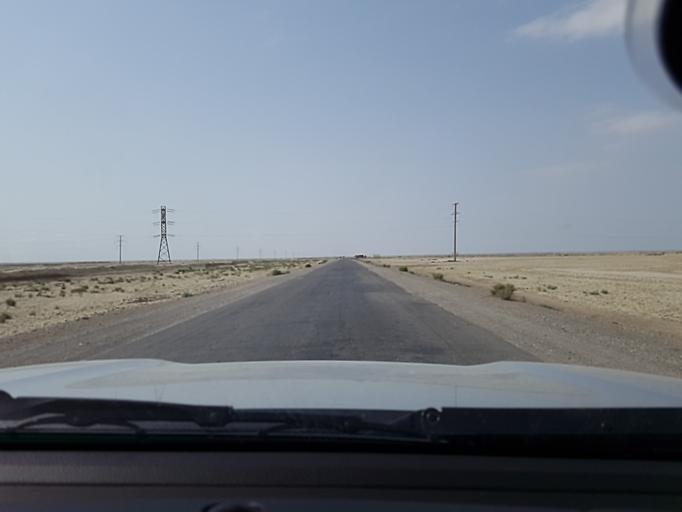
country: TM
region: Balkan
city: Gumdag
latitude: 39.0018
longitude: 54.5861
